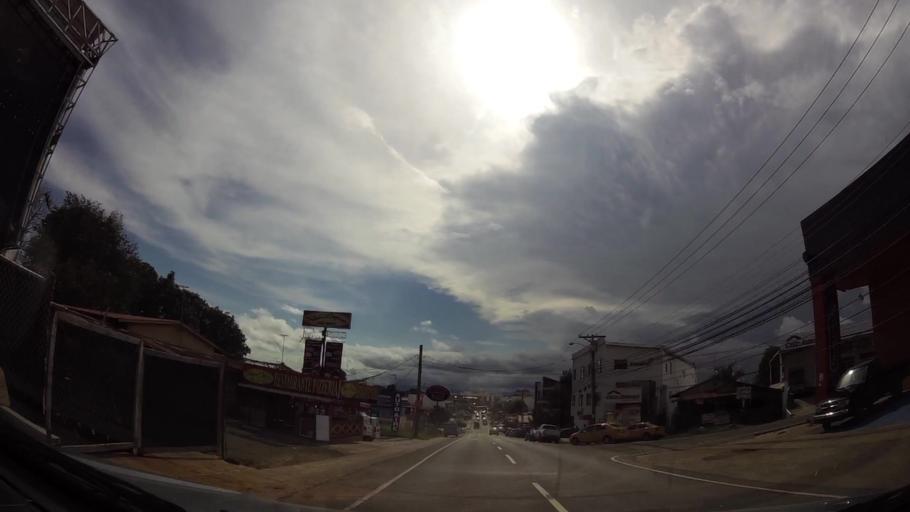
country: PA
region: Panama
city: La Chorrera
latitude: 8.8827
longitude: -79.7780
